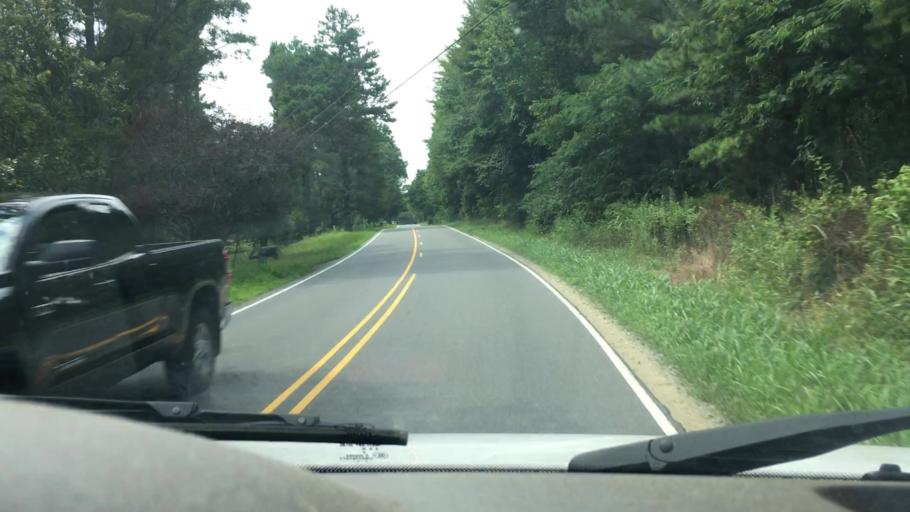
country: US
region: North Carolina
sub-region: Gaston County
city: Davidson
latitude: 35.4807
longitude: -80.8058
